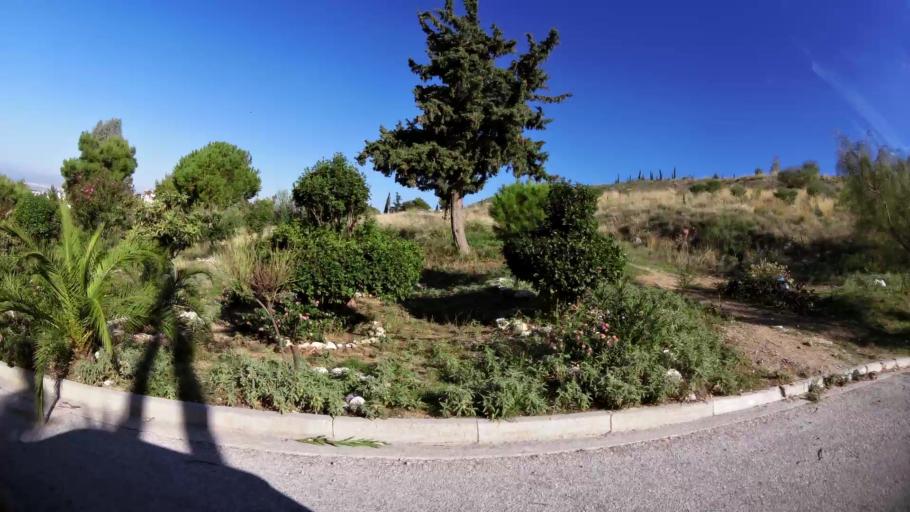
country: GR
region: Attica
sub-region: Nomarchia Athinas
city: Glyfada
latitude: 37.8628
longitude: 23.7716
